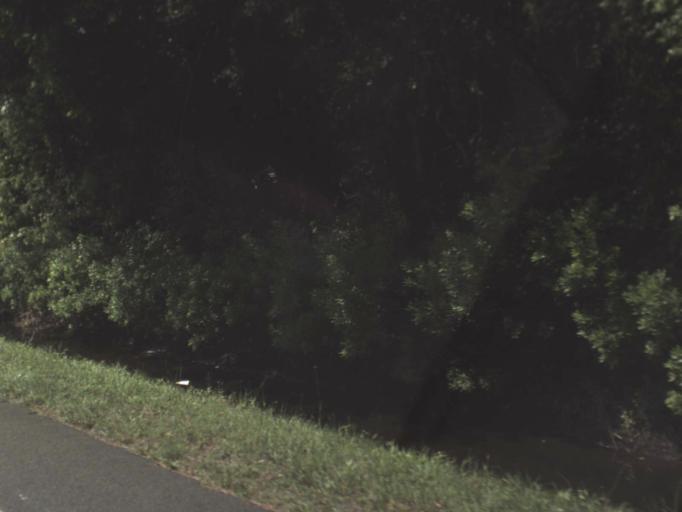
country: US
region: Florida
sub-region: Nassau County
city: Nassau Village-Ratliff
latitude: 30.4846
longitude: -81.7209
